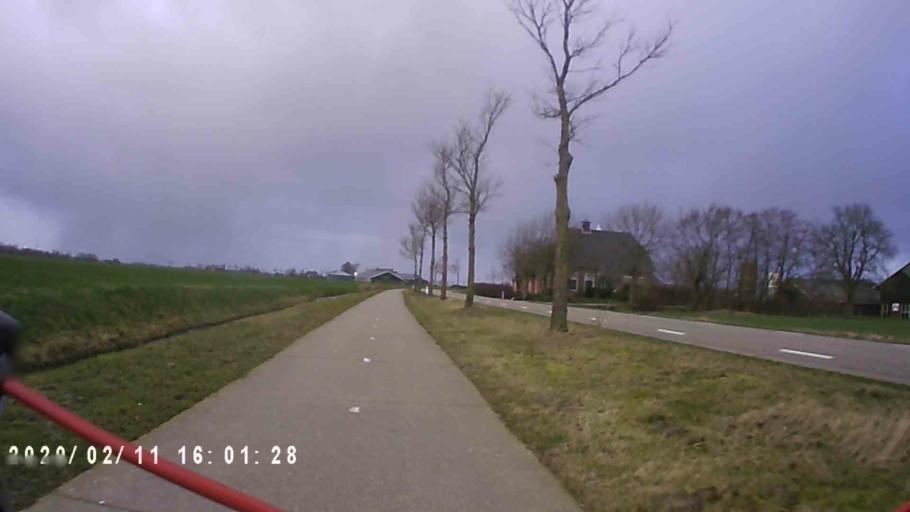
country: NL
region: Groningen
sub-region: Gemeente Zuidhorn
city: Oldehove
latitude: 53.2964
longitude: 6.4214
